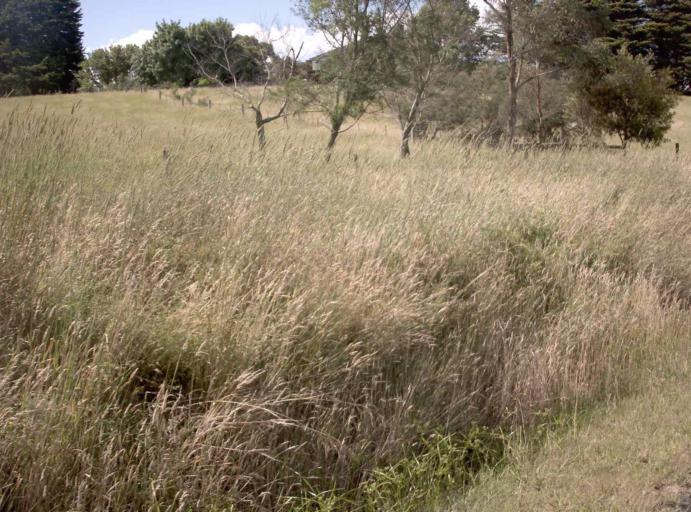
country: AU
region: Victoria
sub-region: Latrobe
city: Morwell
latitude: -38.1504
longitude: 146.4390
